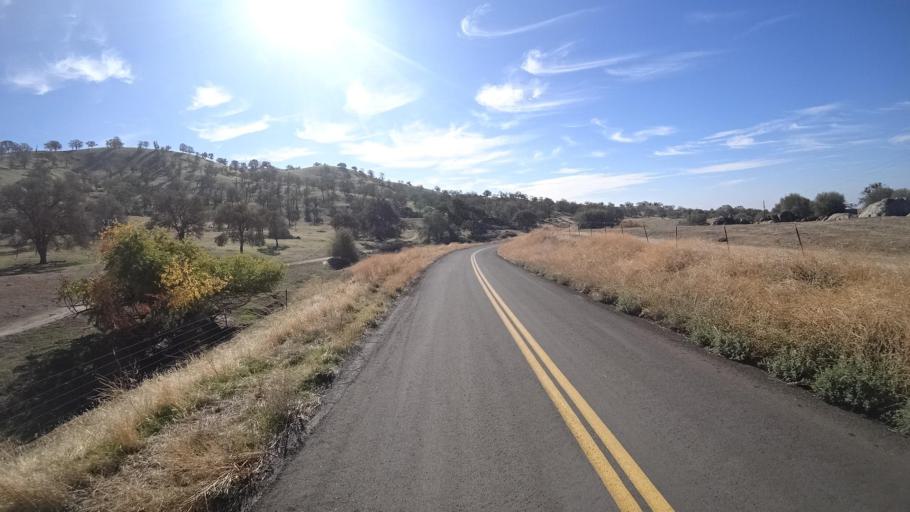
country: US
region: California
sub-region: Kern County
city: Oildale
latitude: 35.6354
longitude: -118.8390
